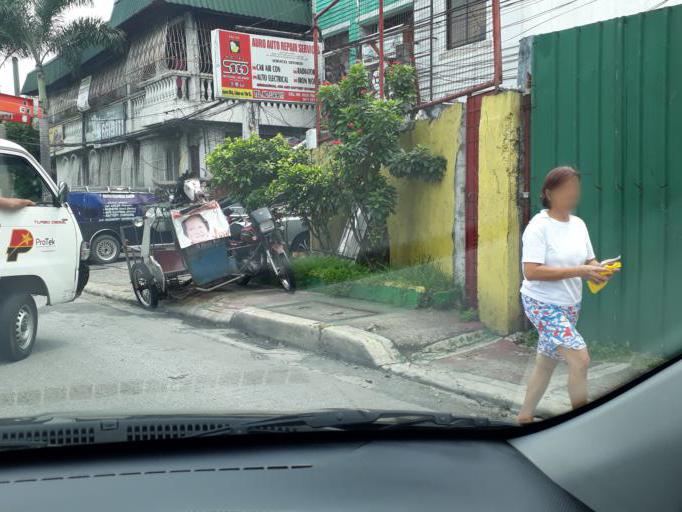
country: PH
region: Metro Manila
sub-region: Quezon City
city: Quezon City
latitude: 14.6300
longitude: 121.0504
